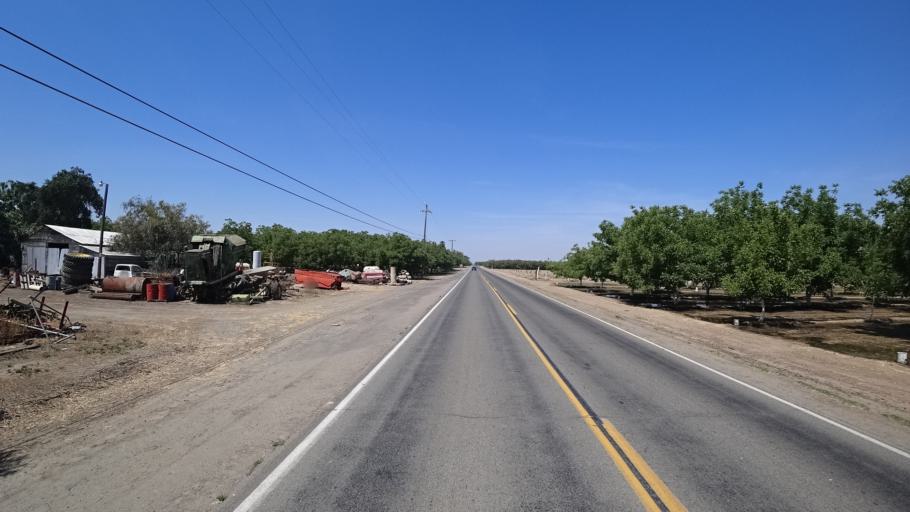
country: US
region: California
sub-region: Fresno County
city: Laton
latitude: 36.4020
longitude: -119.7629
